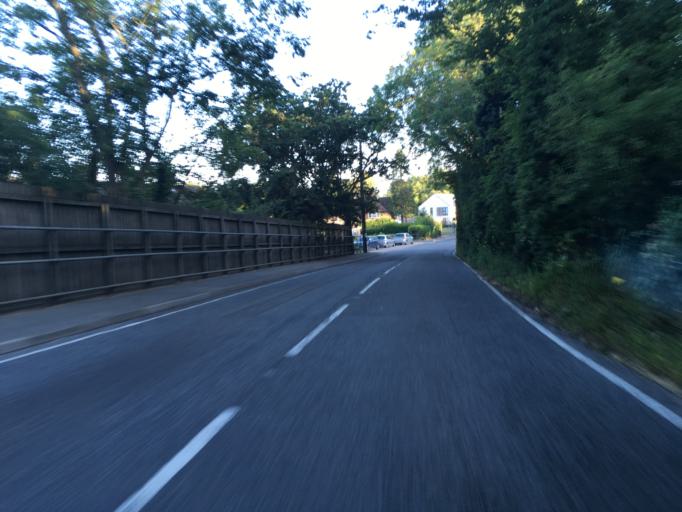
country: GB
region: England
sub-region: Hampshire
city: Tadley
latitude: 51.4022
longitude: -1.1356
